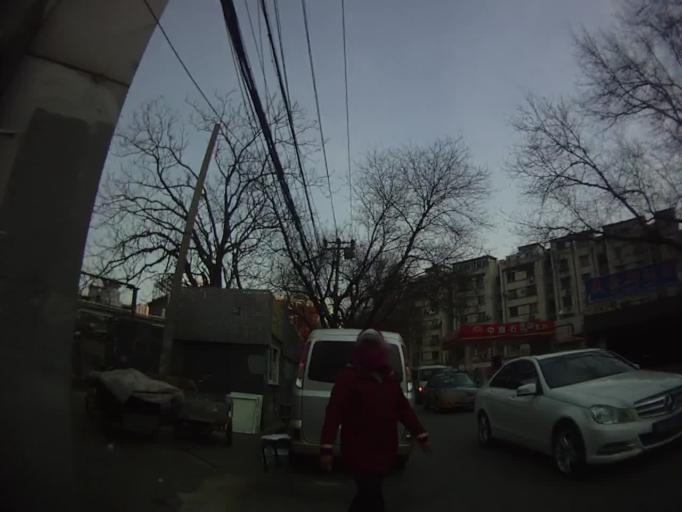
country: CN
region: Beijing
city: Chaowai
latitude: 39.9058
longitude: 116.4396
